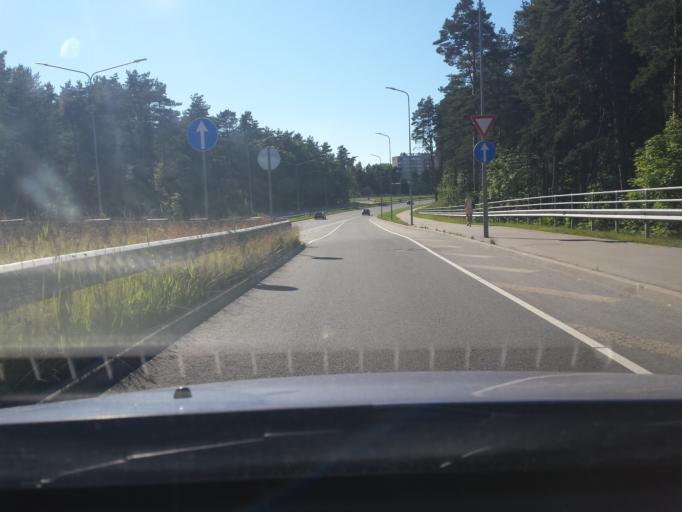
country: LV
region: Riga
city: Jaunciems
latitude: 56.9980
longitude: 24.1374
